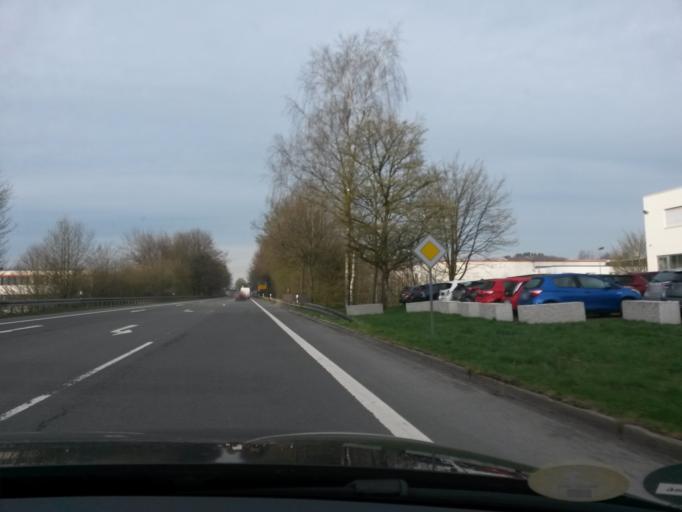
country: DE
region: North Rhine-Westphalia
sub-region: Regierungsbezirk Arnsberg
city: Luedenscheid
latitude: 51.2507
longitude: 7.5985
